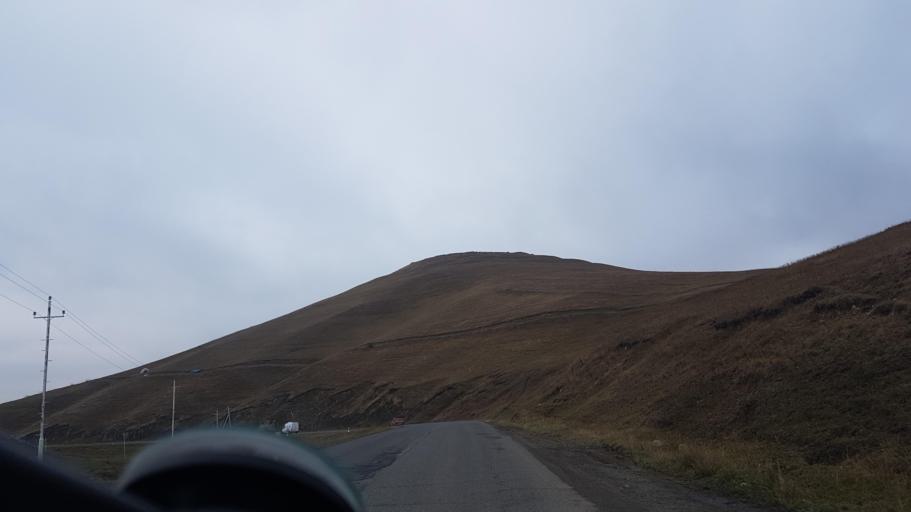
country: AZ
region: Gadabay Rayon
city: Ariqdam
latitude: 40.6179
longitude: 45.8111
